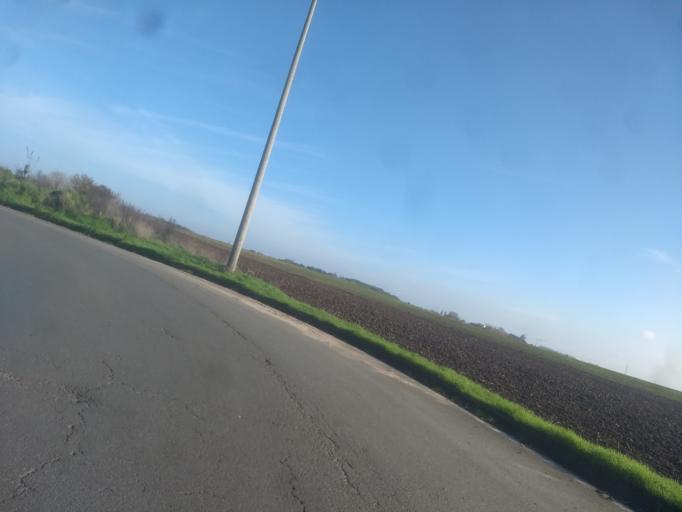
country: FR
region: Nord-Pas-de-Calais
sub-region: Departement du Pas-de-Calais
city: Beaurains
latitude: 50.2774
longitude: 2.7988
